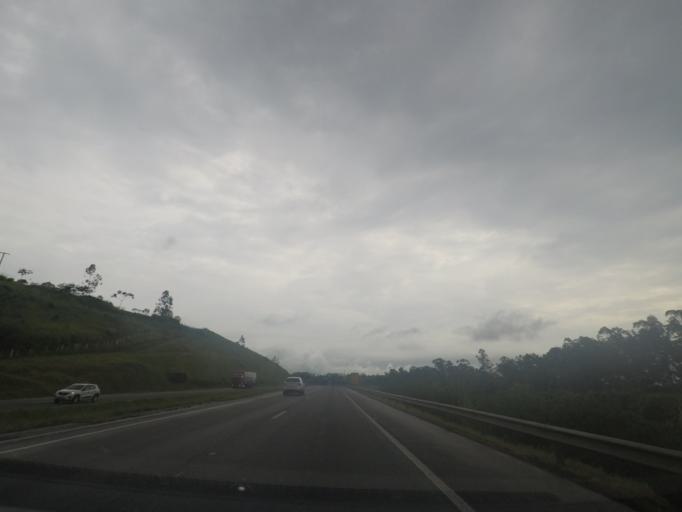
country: BR
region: Sao Paulo
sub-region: Cajati
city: Cajati
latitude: -24.7266
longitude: -48.0907
